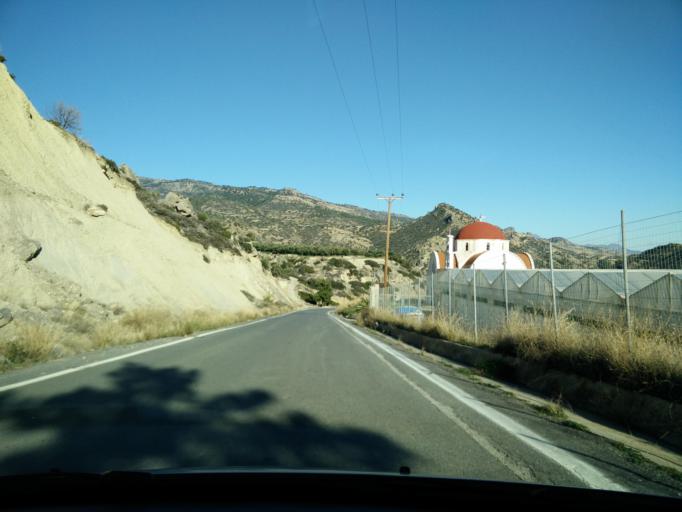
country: GR
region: Crete
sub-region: Nomos Lasithiou
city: Gra Liyia
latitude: 35.0156
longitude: 25.5791
